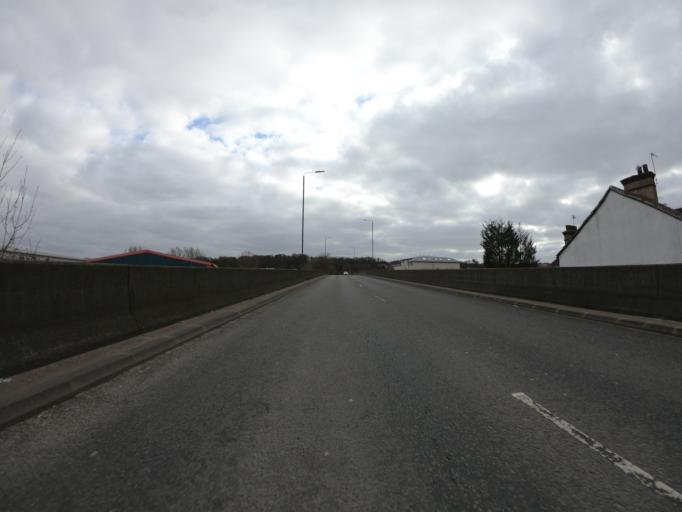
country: GB
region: England
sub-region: Greater London
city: Belvedere
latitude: 51.4933
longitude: 0.1564
